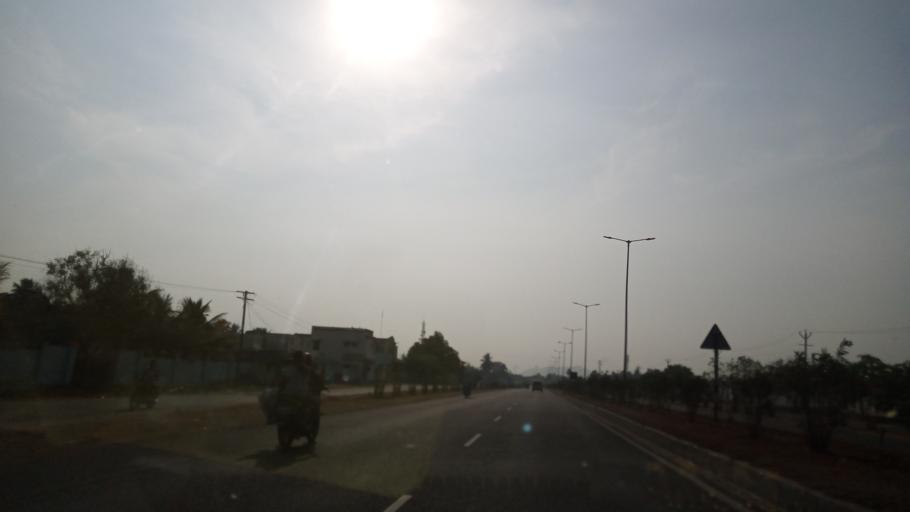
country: IN
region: Tamil Nadu
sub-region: Salem
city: Belur
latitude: 11.6532
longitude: 78.3449
